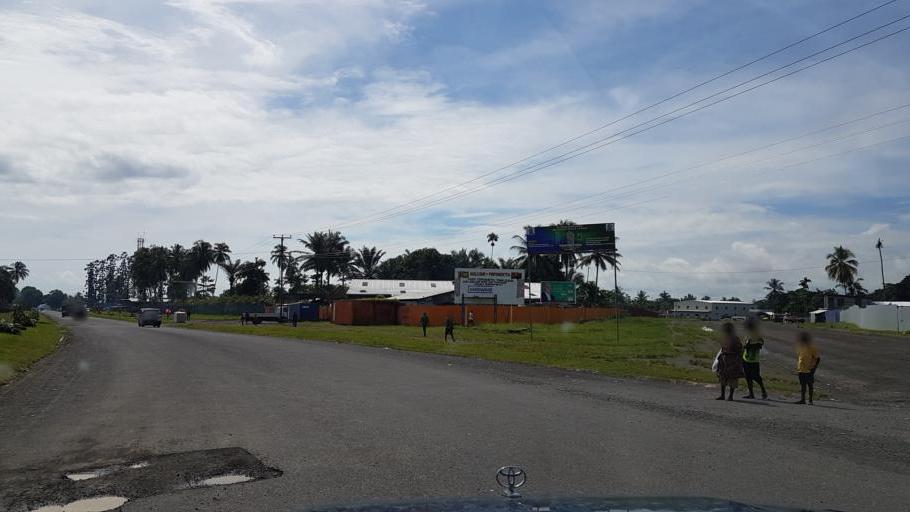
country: PG
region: Northern Province
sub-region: Sohe
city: Popondetta
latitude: -8.7694
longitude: 148.2331
